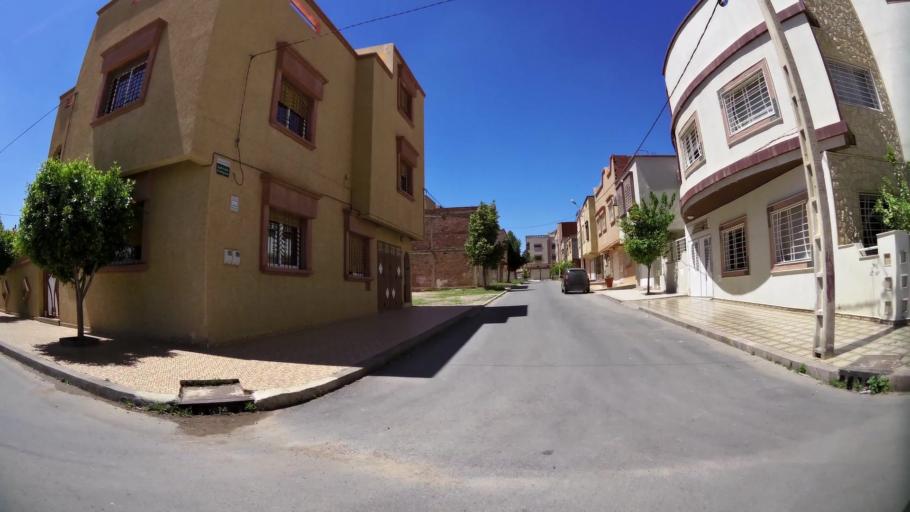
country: MA
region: Oriental
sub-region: Oujda-Angad
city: Oujda
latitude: 34.6616
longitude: -1.9468
